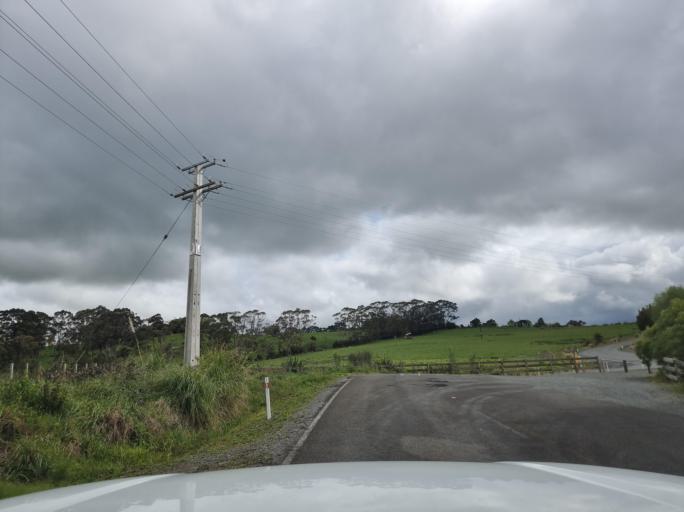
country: NZ
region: Northland
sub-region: Whangarei
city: Ruakaka
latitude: -36.1227
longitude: 174.1899
